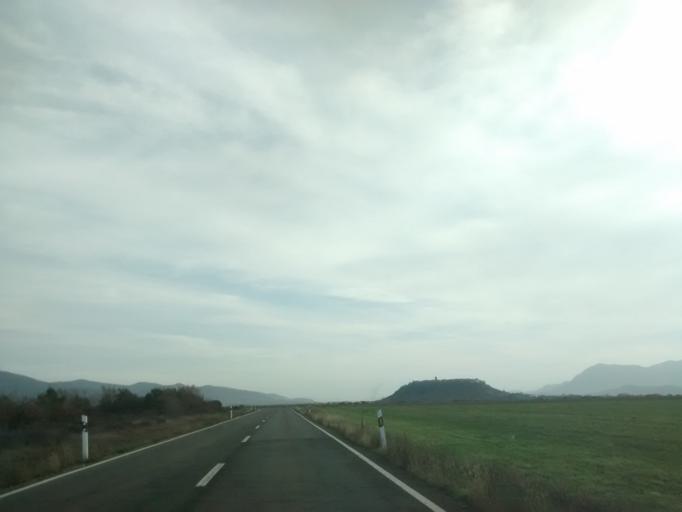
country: ES
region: Aragon
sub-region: Provincia de Zaragoza
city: Mianos
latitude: 42.6106
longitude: -0.8844
